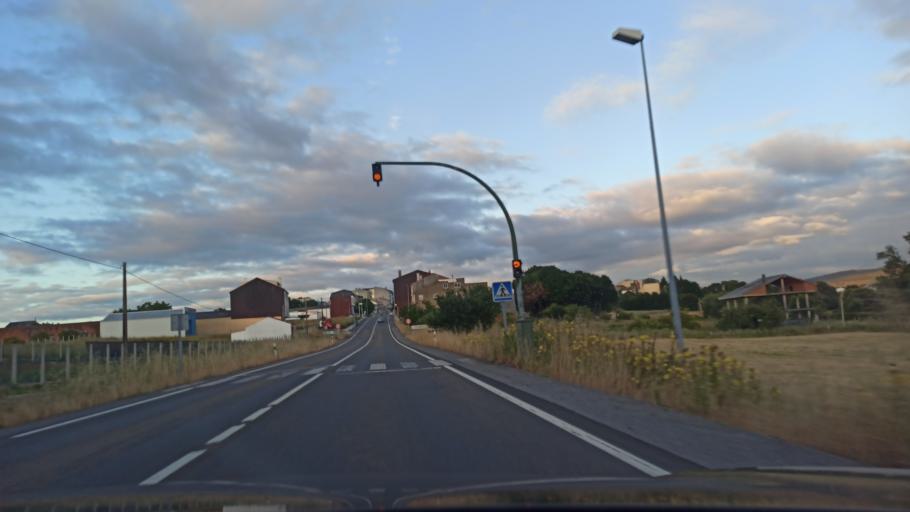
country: ES
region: Galicia
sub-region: Provincia de Lugo
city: Monterroso
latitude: 42.7926
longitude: -7.8458
